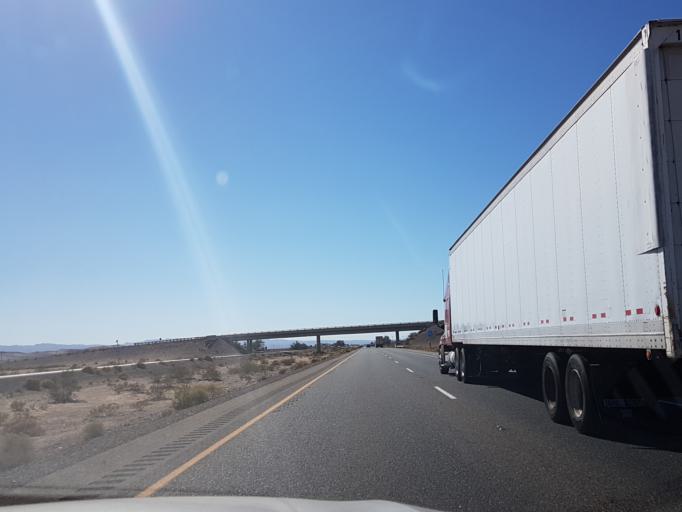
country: US
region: California
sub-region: San Bernardino County
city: Fort Irwin
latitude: 34.9649
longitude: -116.6423
